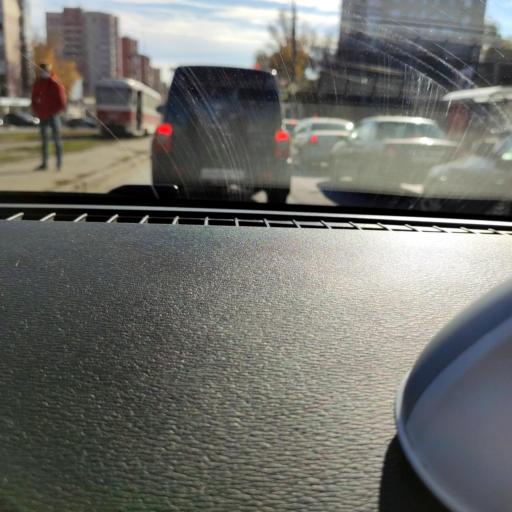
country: RU
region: Samara
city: Samara
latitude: 53.2355
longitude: 50.2195
